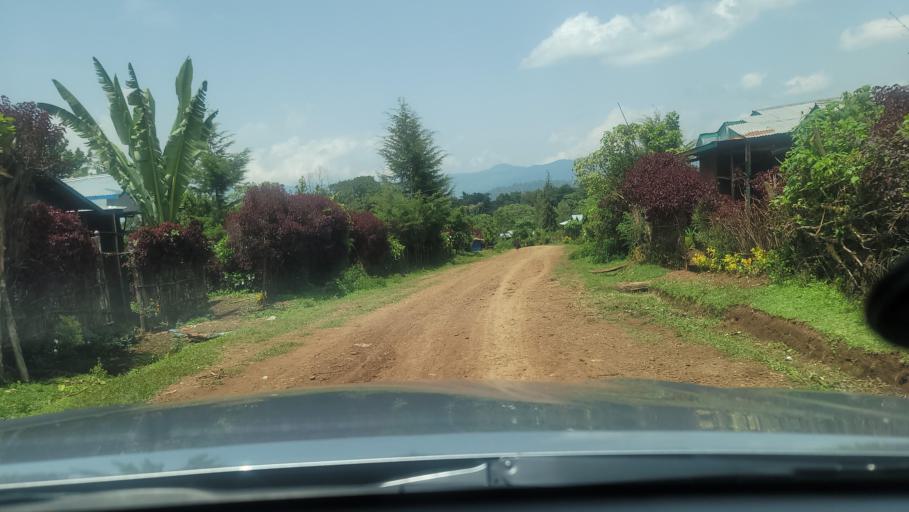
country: ET
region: Oromiya
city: Agaro
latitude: 7.7976
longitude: 36.4170
